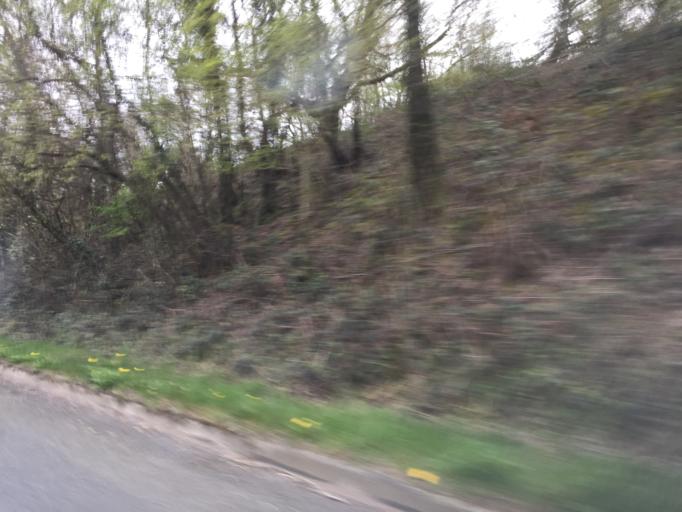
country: GB
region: Wales
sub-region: Caerphilly County Borough
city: Caerphilly
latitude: 51.5618
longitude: -3.2303
